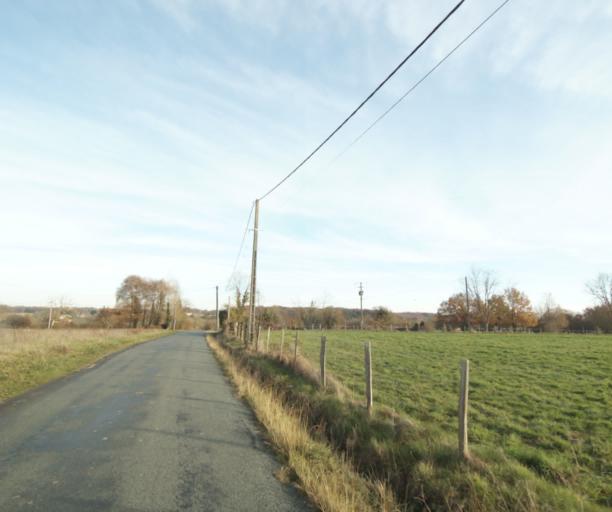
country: FR
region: Poitou-Charentes
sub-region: Departement de la Charente-Maritime
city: Chaniers
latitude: 45.7456
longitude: -0.5479
